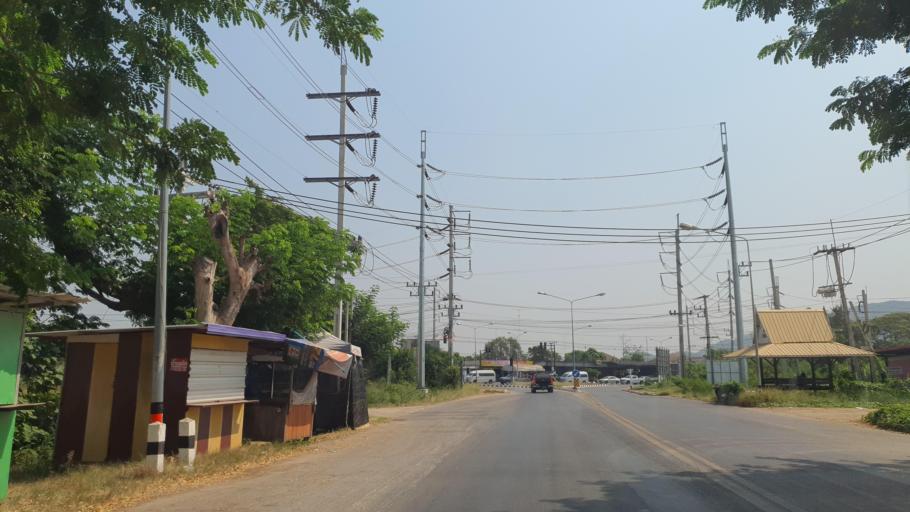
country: TH
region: Kanchanaburi
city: Kanchanaburi
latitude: 14.0590
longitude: 99.4773
